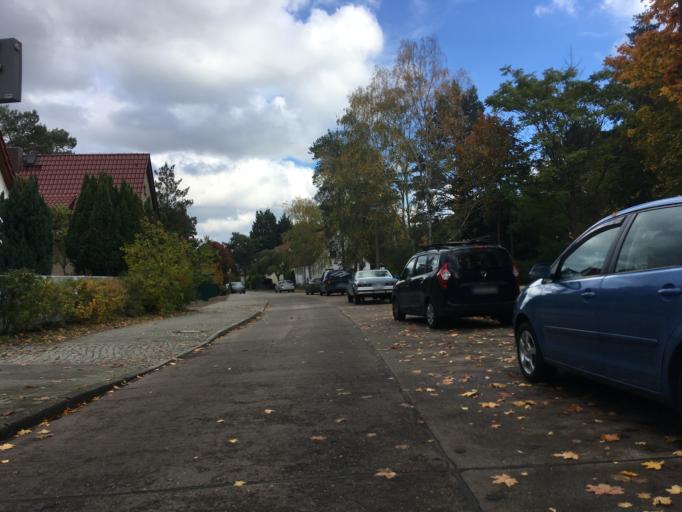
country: DE
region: Berlin
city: Oberschoneweide
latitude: 52.4484
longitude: 13.5315
